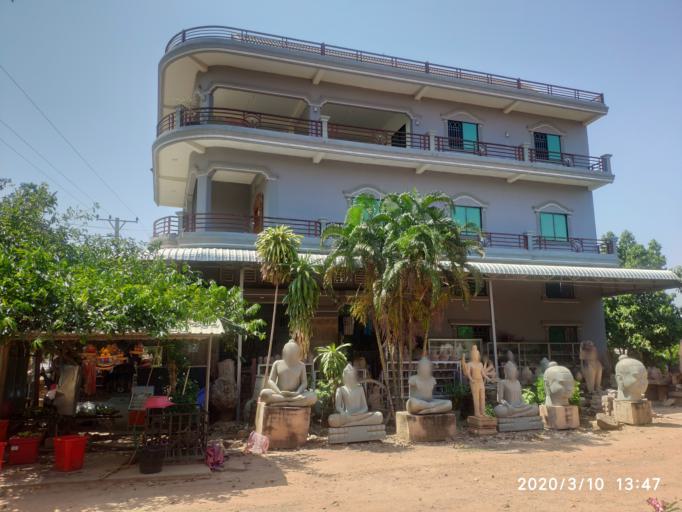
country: KH
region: Banteay Meanchey
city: Sisophon
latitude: 13.6269
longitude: 103.1635
